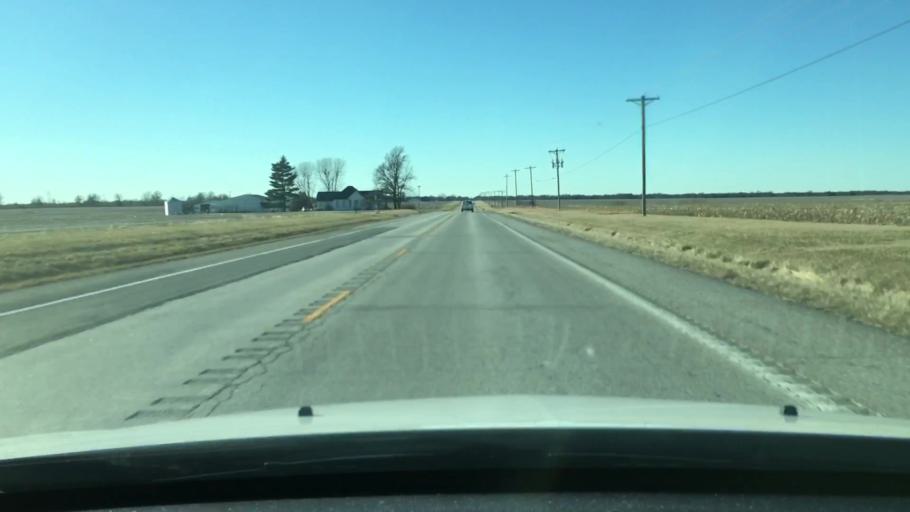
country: US
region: Missouri
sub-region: Audrain County
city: Vandalia
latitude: 39.3459
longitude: -91.3625
